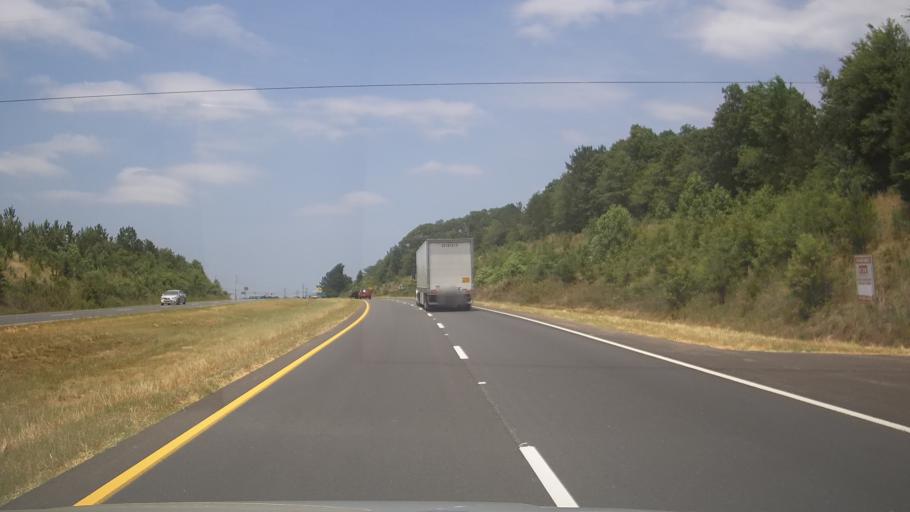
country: US
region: Georgia
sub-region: Jackson County
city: Commerce
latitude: 34.2296
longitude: -83.4505
